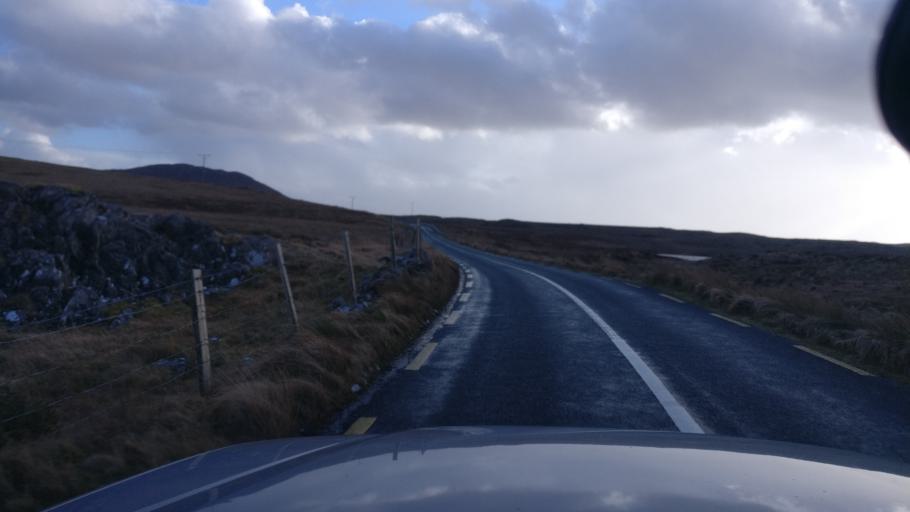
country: IE
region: Connaught
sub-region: County Galway
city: Clifden
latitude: 53.4412
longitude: -9.7711
